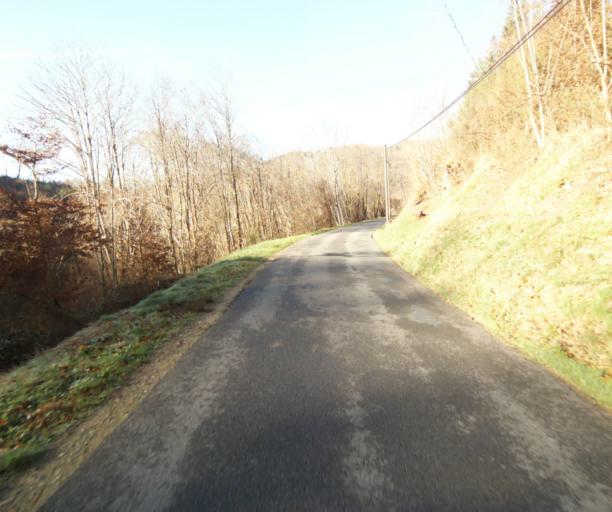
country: FR
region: Limousin
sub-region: Departement de la Correze
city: Chameyrat
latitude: 45.2348
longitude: 1.7331
